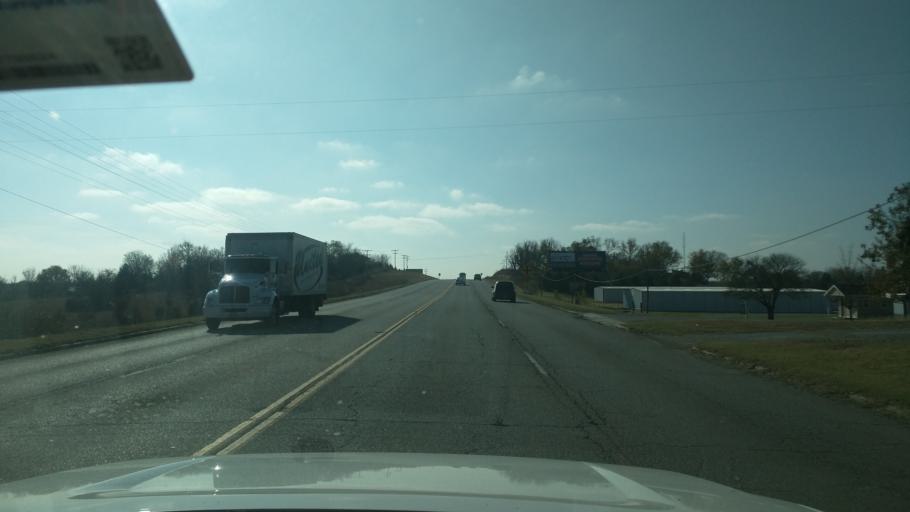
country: US
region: Oklahoma
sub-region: Washington County
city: Bartlesville
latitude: 36.6885
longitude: -95.9351
